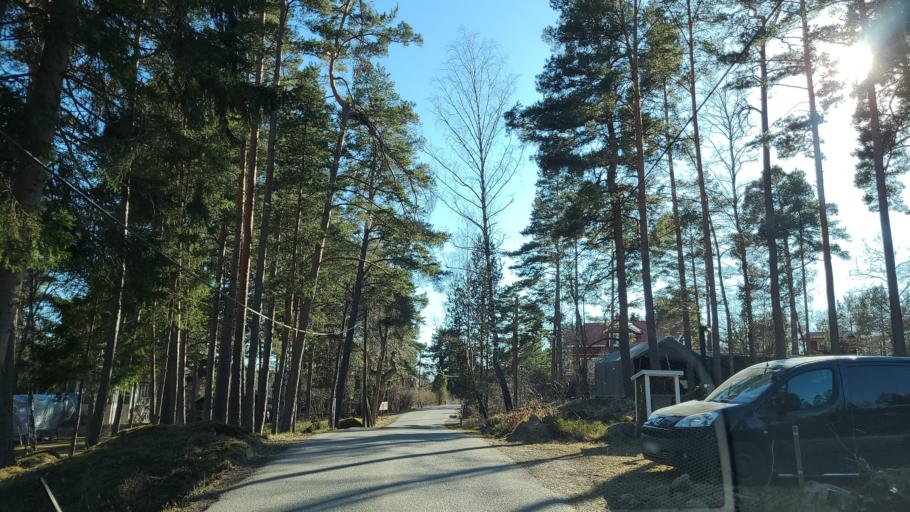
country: SE
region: Stockholm
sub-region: Varmdo Kommun
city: Holo
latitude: 59.3613
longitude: 18.6564
